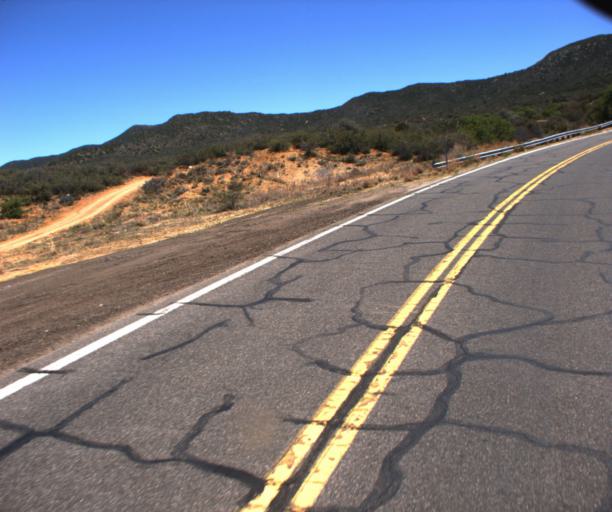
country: US
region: Arizona
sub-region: Yavapai County
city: Prescott
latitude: 34.4276
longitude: -112.5835
